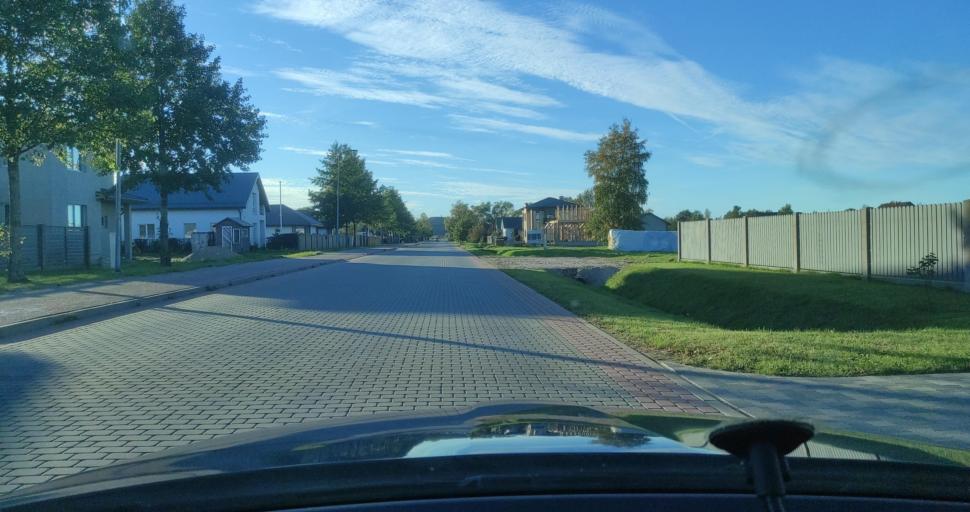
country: LV
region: Ventspils
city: Ventspils
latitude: 57.3657
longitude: 21.5724
